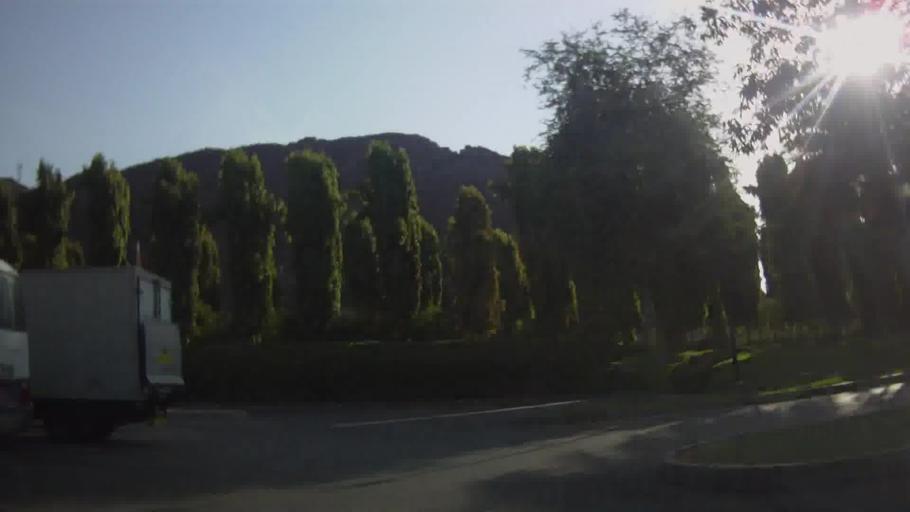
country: OM
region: Muhafazat Masqat
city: Muscat
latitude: 23.5674
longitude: 58.6138
